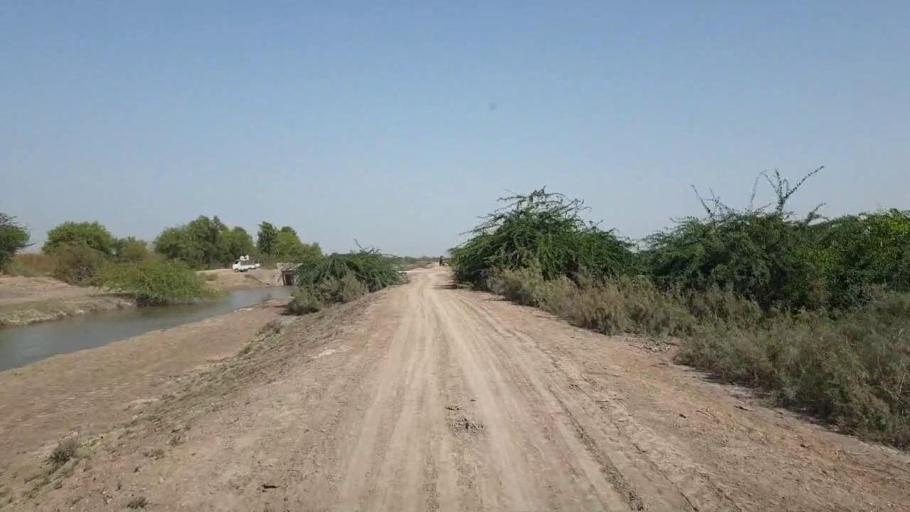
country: PK
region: Sindh
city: Tando Bago
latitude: 24.6680
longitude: 69.0681
